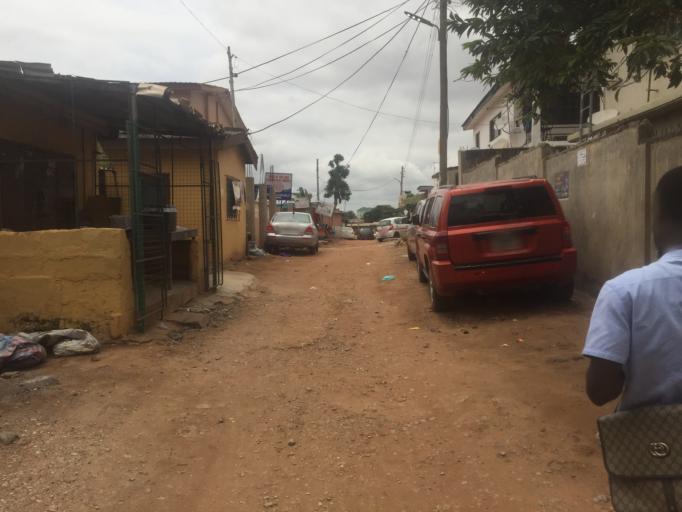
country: GH
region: Greater Accra
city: Dome
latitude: 5.6037
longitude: -0.2437
